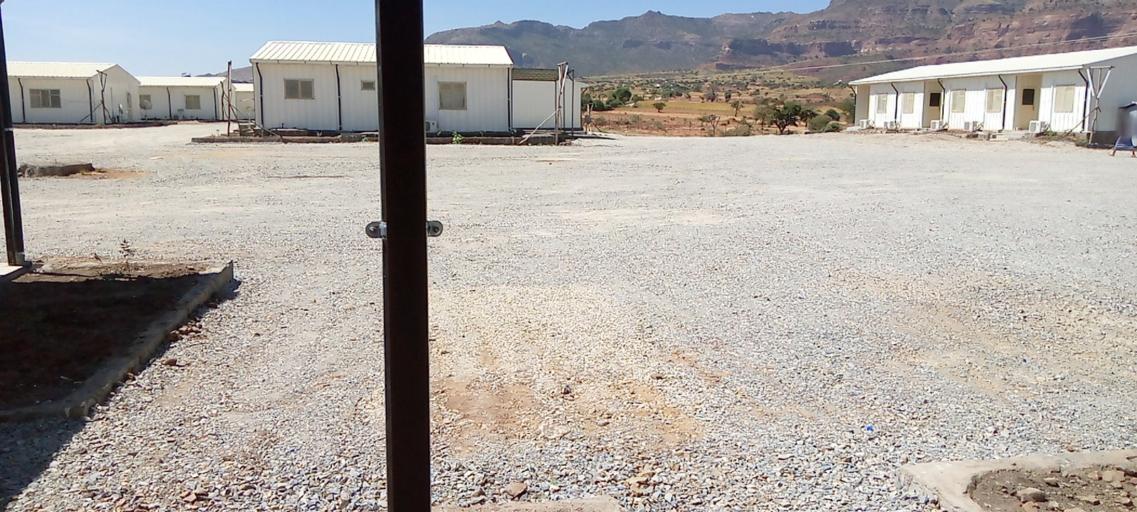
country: ET
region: Tigray
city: Mekele
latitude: 13.2446
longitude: 38.9944
